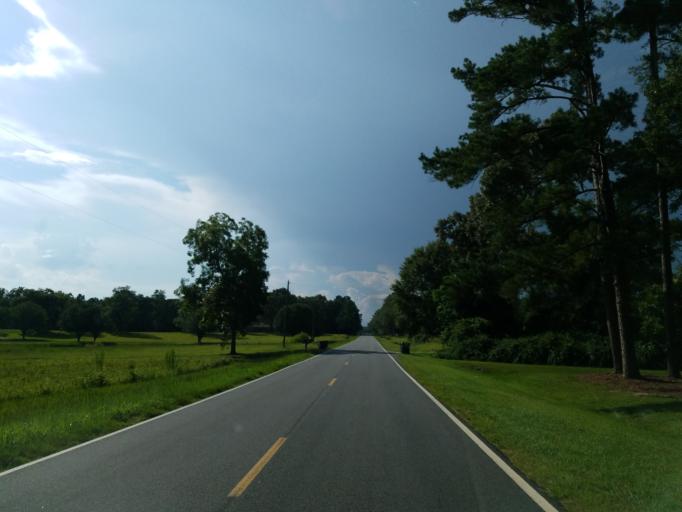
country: US
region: Georgia
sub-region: Lowndes County
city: Hahira
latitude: 31.0229
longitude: -83.4366
